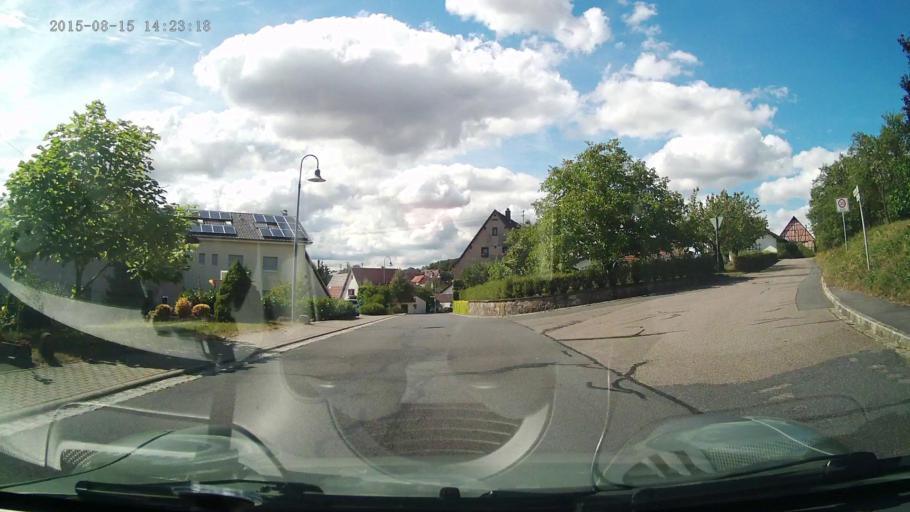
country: DE
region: Baden-Wuerttemberg
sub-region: Karlsruhe Region
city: Seckach
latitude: 49.4531
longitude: 9.3707
